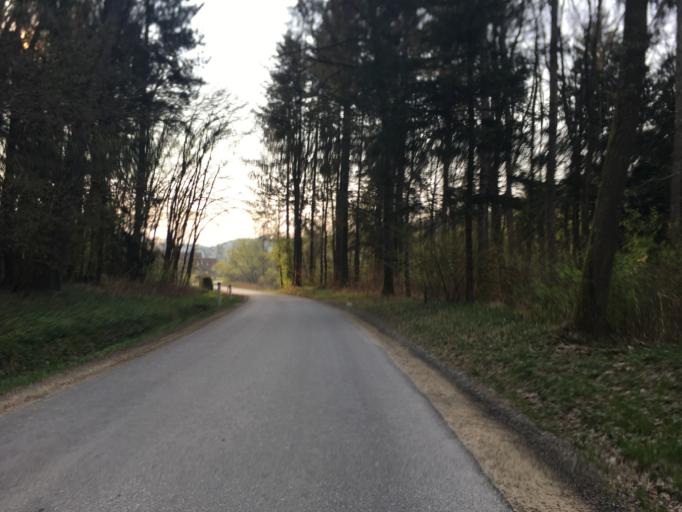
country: AT
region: Styria
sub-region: Politischer Bezirk Graz-Umgebung
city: Nestelbach bei Graz
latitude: 47.0791
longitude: 15.6303
